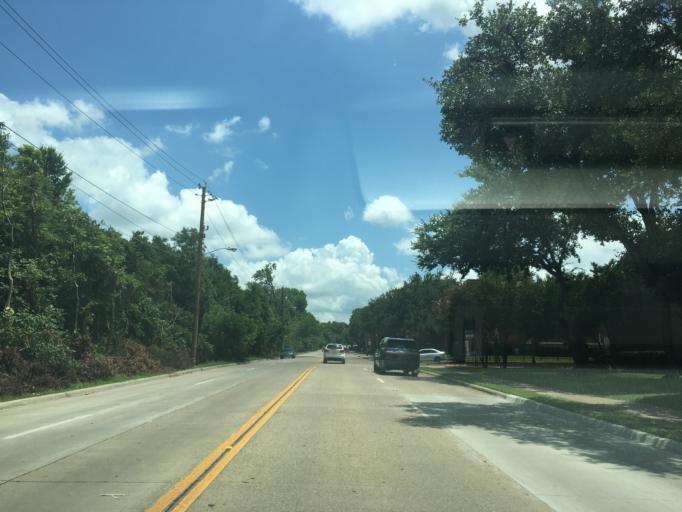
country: US
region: Texas
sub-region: Dallas County
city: University Park
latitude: 32.8734
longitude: -96.7528
